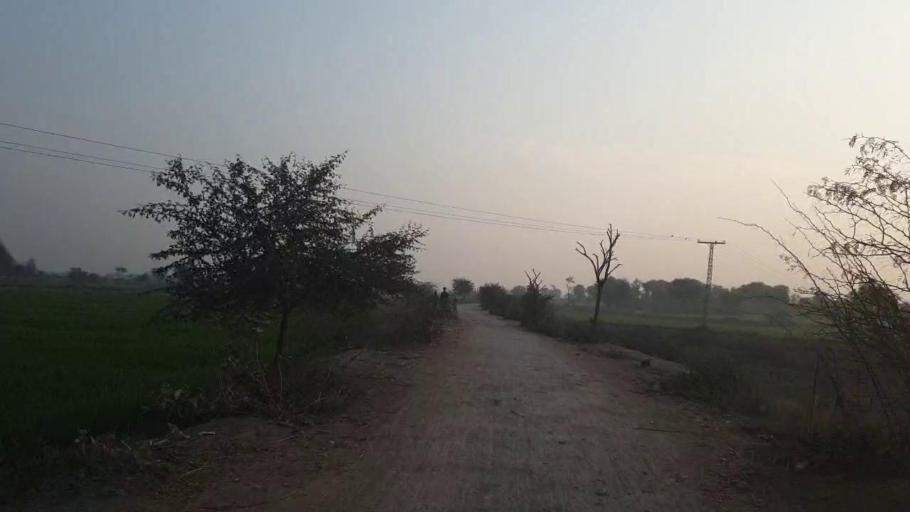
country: PK
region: Sindh
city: Bhit Shah
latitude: 25.7702
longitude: 68.4611
